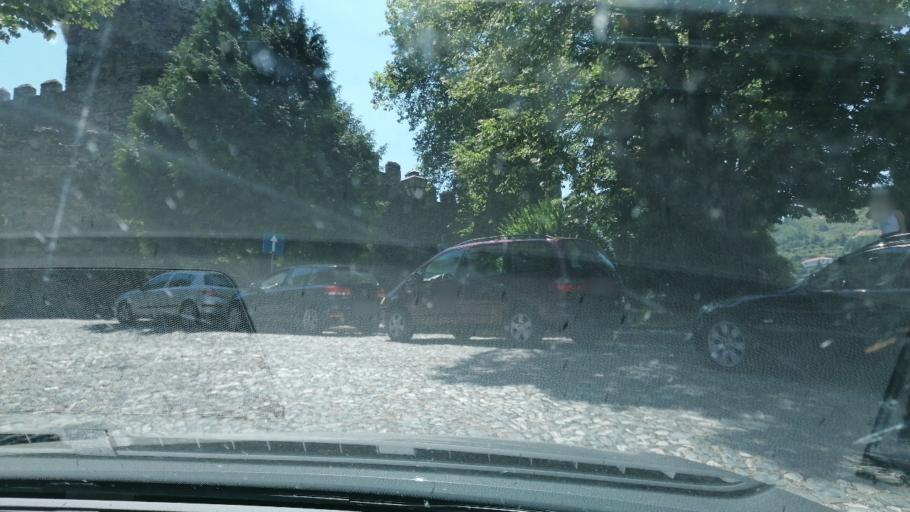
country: PT
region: Braganca
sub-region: Braganca Municipality
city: Braganca
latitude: 41.8041
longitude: -6.7512
